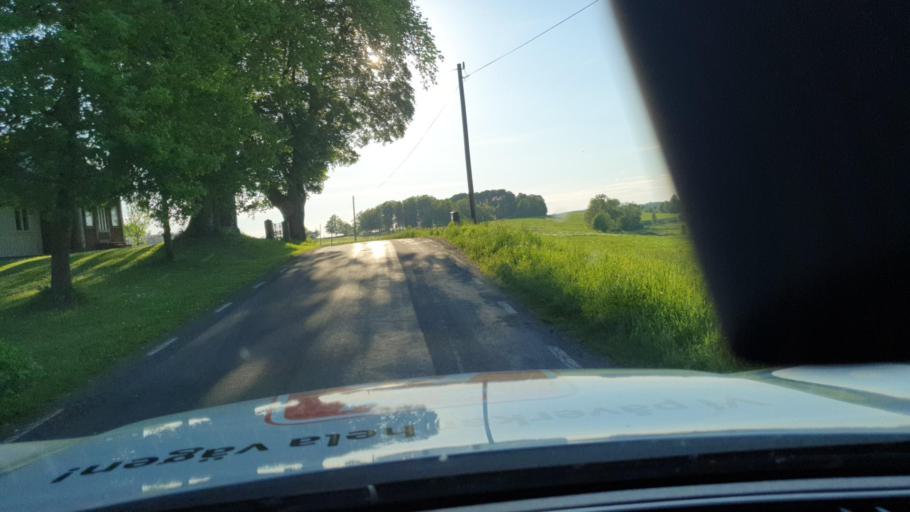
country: SE
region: Vaestra Goetaland
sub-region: Falkopings Kommun
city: Falkoeping
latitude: 58.0835
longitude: 13.5948
